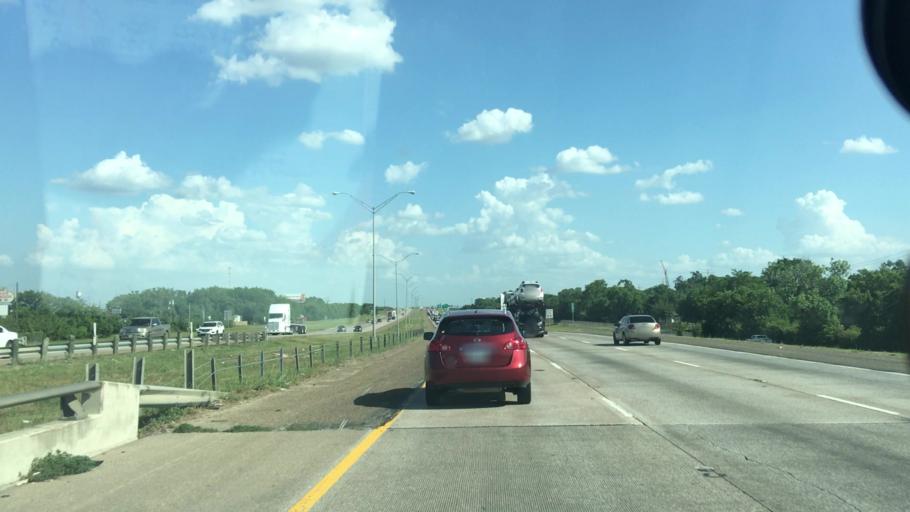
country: US
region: Texas
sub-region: Dallas County
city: Dallas
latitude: 32.7241
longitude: -96.7621
